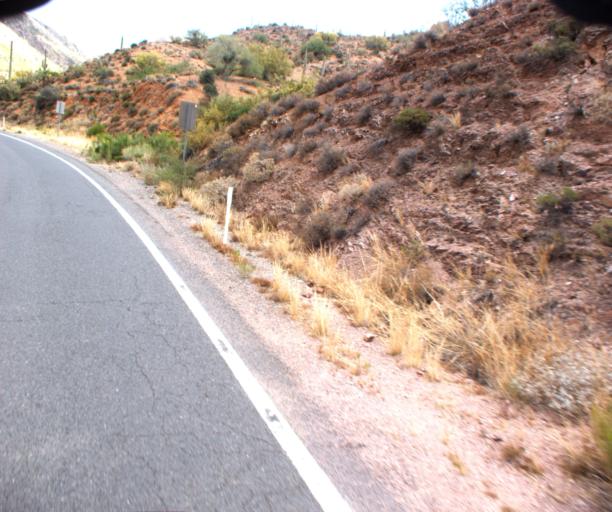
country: US
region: Arizona
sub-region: Pinal County
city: Superior
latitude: 33.1913
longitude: -111.0442
